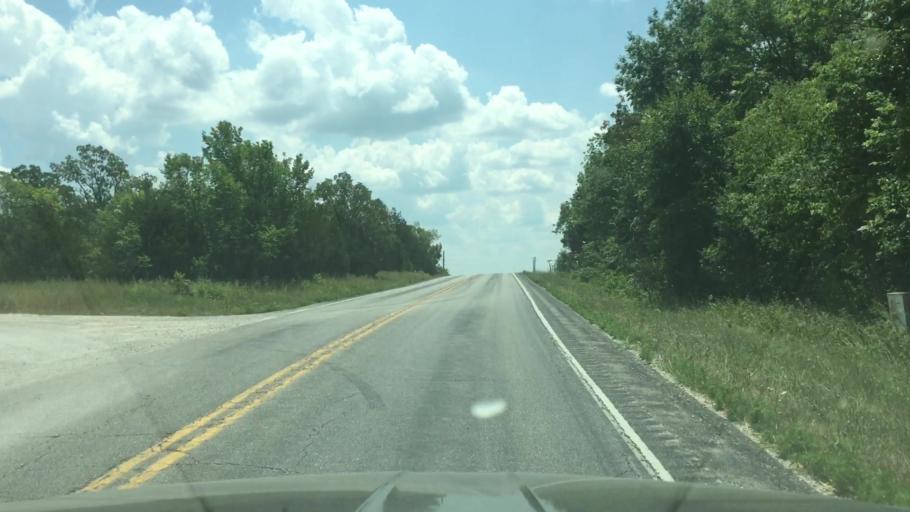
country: US
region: Missouri
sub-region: Miller County
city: Tuscumbia
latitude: 38.1150
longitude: -92.5082
